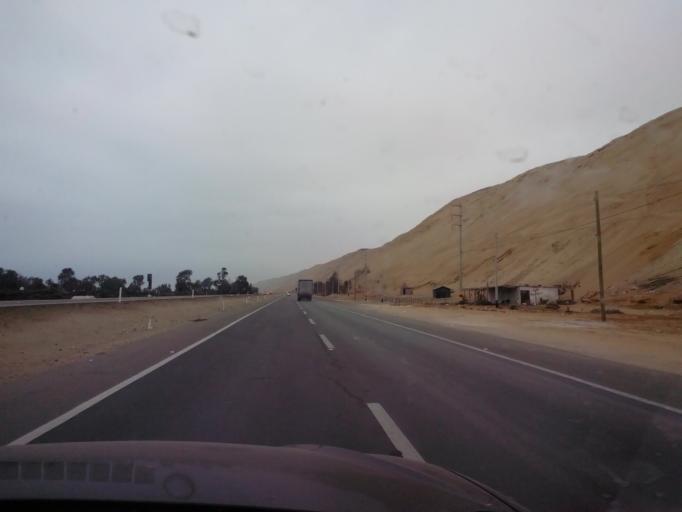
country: PE
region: Ica
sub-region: Provincia de Chincha
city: San Pedro
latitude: -13.3760
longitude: -76.2079
